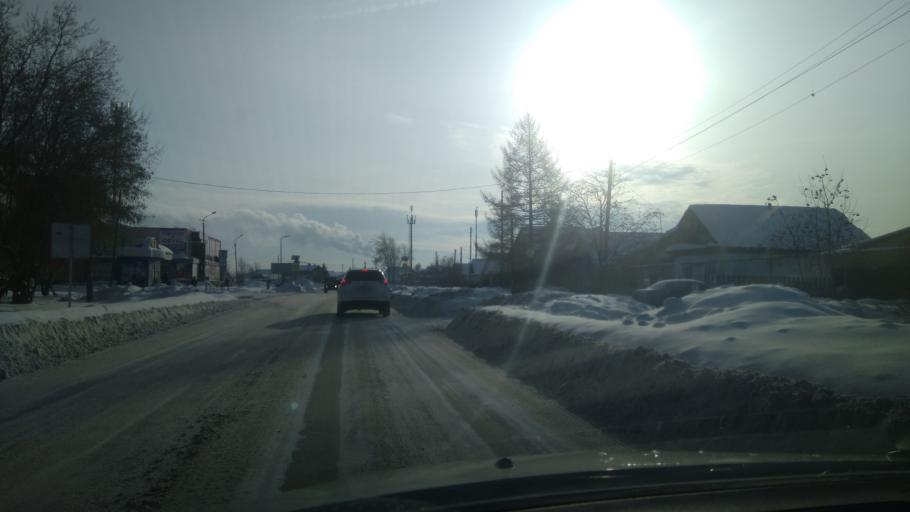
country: RU
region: Sverdlovsk
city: Sukhoy Log
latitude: 56.8937
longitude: 62.0333
